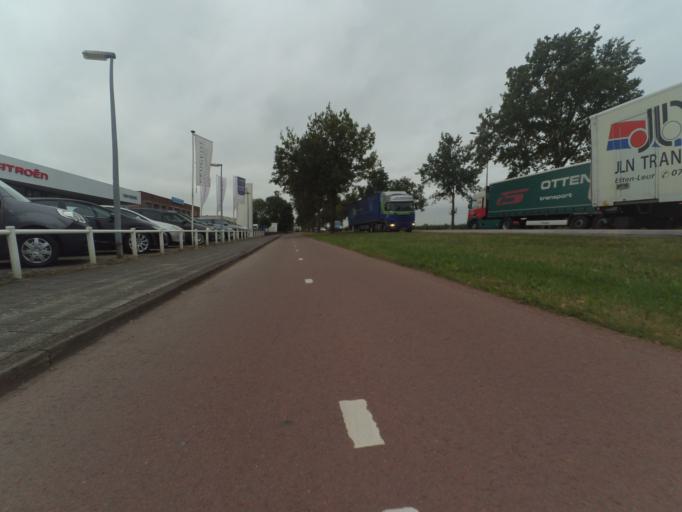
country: NL
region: Gelderland
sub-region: Gemeente Tiel
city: Tiel
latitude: 51.9149
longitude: 5.4250
